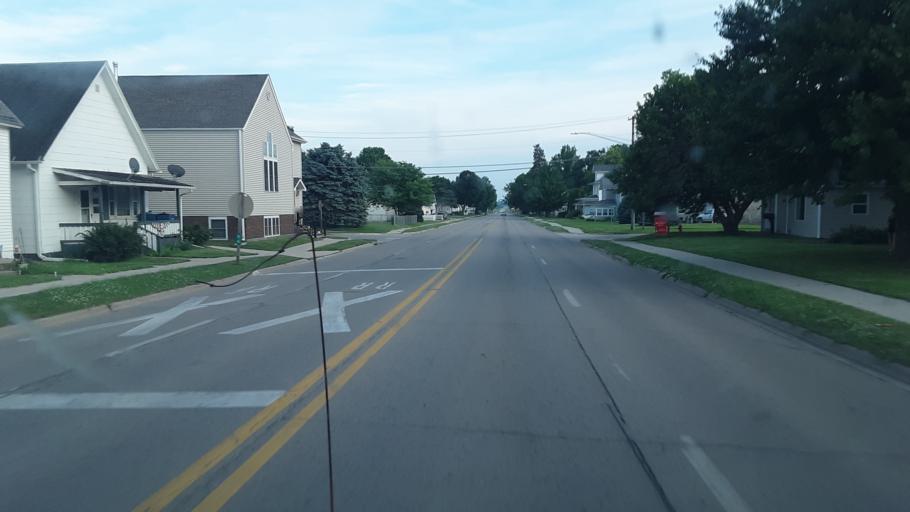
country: US
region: Iowa
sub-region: Benton County
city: Belle Plaine
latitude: 41.8949
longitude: -92.2782
